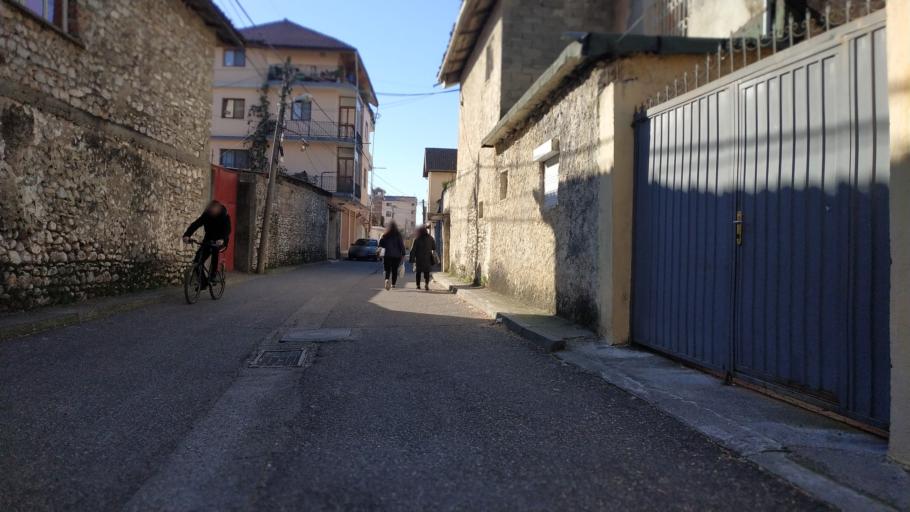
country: AL
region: Shkoder
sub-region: Rrethi i Shkodres
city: Shkoder
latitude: 42.0722
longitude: 19.5140
